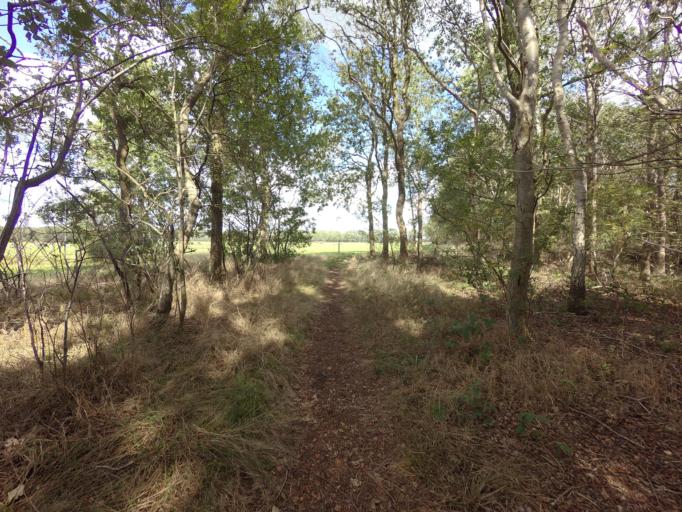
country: NL
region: Friesland
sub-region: Gemeente Weststellingwerf
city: Noordwolde
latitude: 52.9568
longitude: 6.2020
